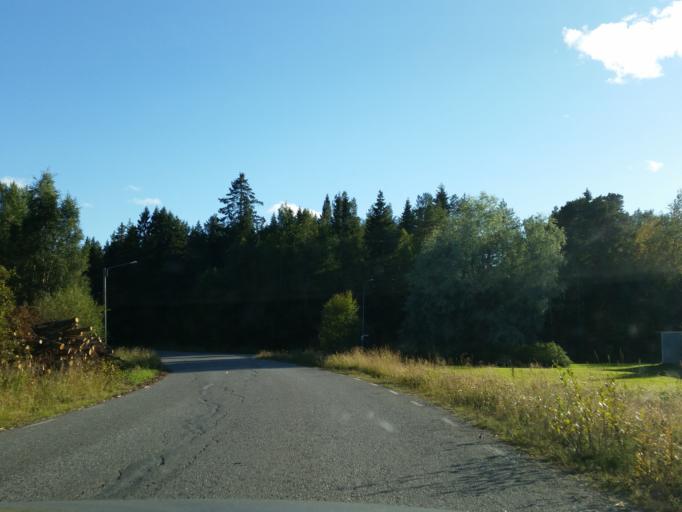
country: SE
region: Vaesterbotten
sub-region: Robertsfors Kommun
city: Robertsfors
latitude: 64.0556
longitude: 20.8539
